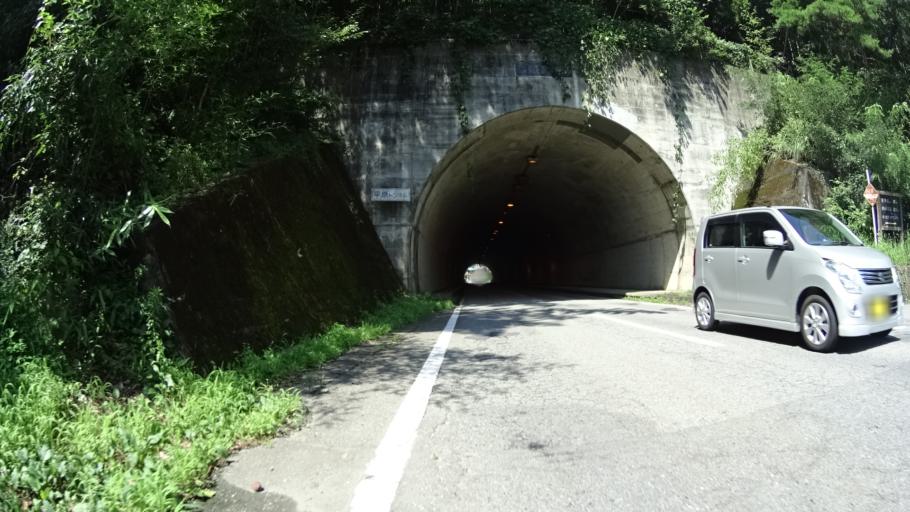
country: JP
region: Gunma
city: Tomioka
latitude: 36.0920
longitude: 138.8170
